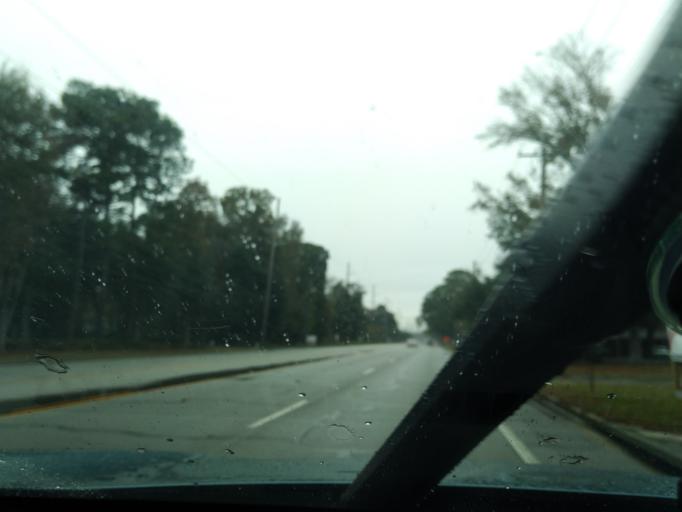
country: US
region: South Carolina
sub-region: Charleston County
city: Charleston
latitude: 32.7242
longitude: -79.9673
